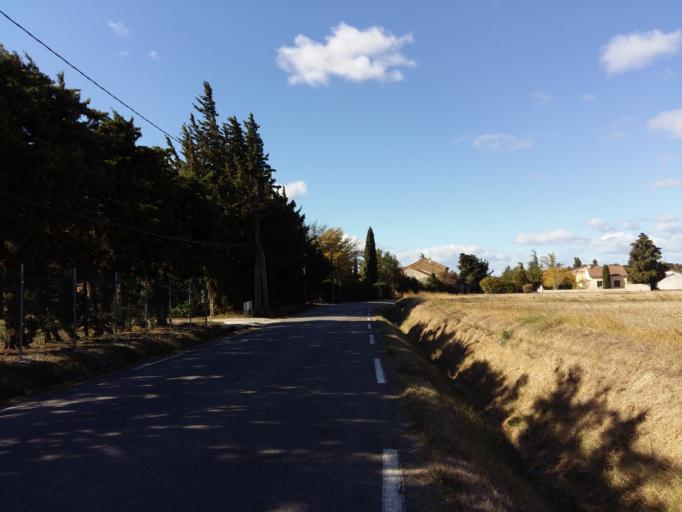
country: FR
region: Provence-Alpes-Cote d'Azur
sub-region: Departement du Vaucluse
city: Piolenc
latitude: 44.1800
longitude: 4.7757
